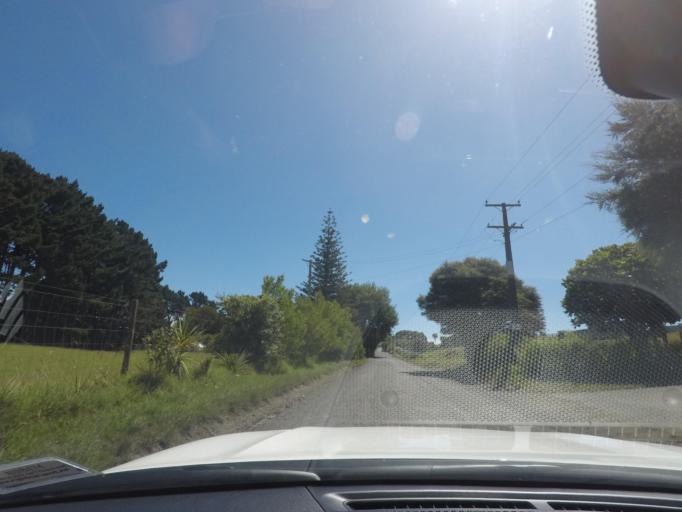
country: NZ
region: Auckland
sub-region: Auckland
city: Parakai
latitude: -36.5808
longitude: 174.3173
